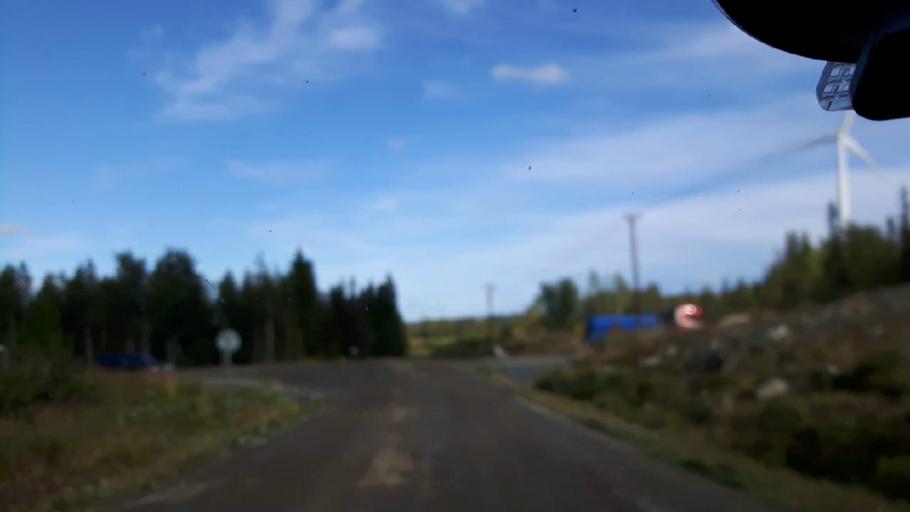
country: SE
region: Jaemtland
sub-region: Ragunda Kommun
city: Hammarstrand
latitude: 63.4252
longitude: 16.1363
